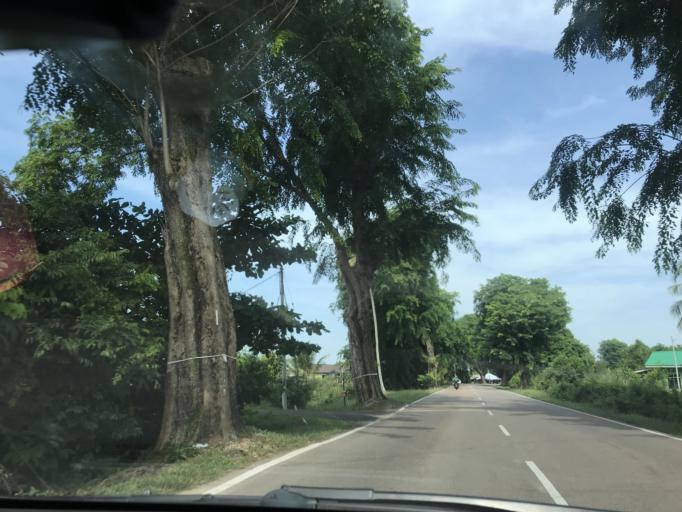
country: MY
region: Kelantan
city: Tumpat
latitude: 6.2017
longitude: 102.1534
